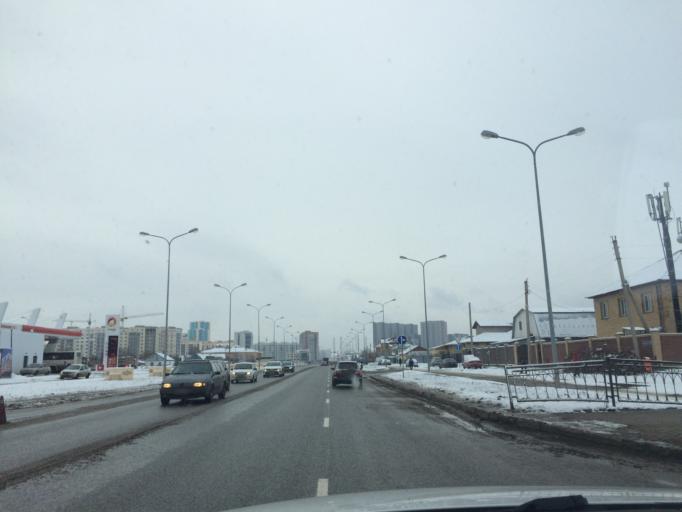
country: KZ
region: Astana Qalasy
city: Astana
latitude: 51.1312
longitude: 71.4944
